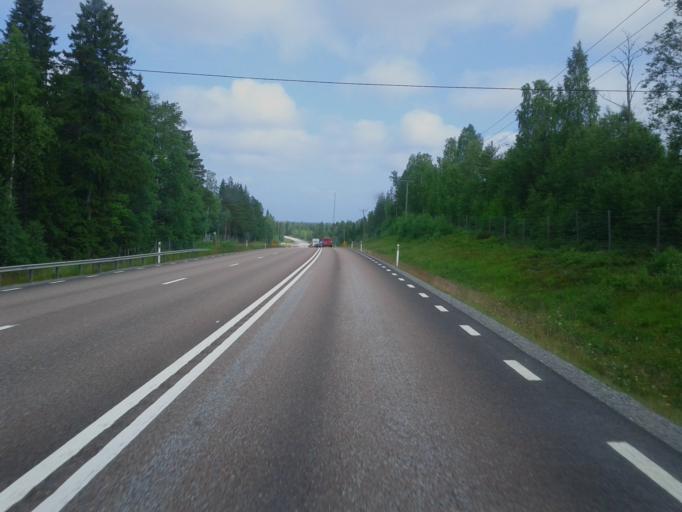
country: SE
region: Vaesterbotten
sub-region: Skelleftea Kommun
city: Burea
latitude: 64.4605
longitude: 21.2906
